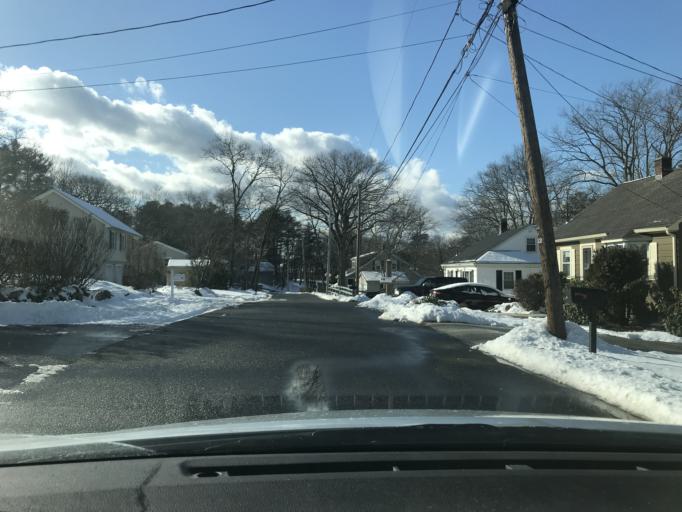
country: US
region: Massachusetts
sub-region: Essex County
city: Saugus
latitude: 42.4881
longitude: -71.0095
